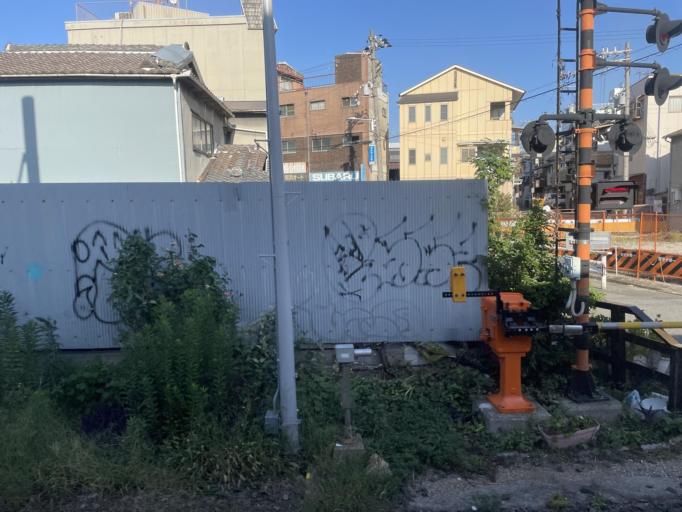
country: JP
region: Osaka
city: Osaka-shi
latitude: 34.6493
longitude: 135.4820
